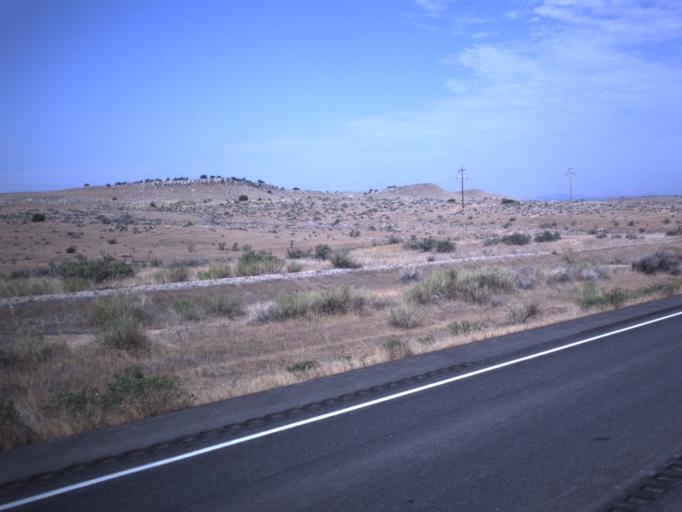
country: US
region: Utah
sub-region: Uintah County
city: Naples
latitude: 40.3373
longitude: -109.2913
